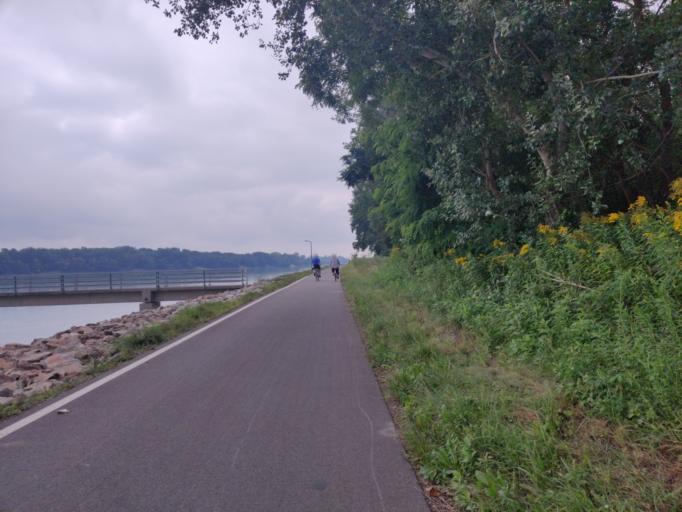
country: AT
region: Lower Austria
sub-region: Politischer Bezirk Tulln
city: Kirchberg am Wagram
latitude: 48.3697
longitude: 15.8708
